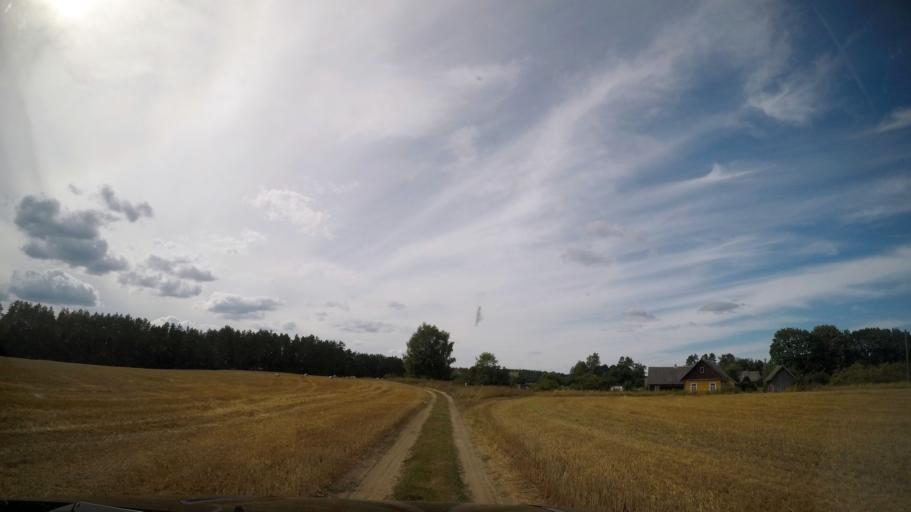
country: BY
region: Grodnenskaya
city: Skidal'
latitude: 53.8397
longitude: 24.1859
